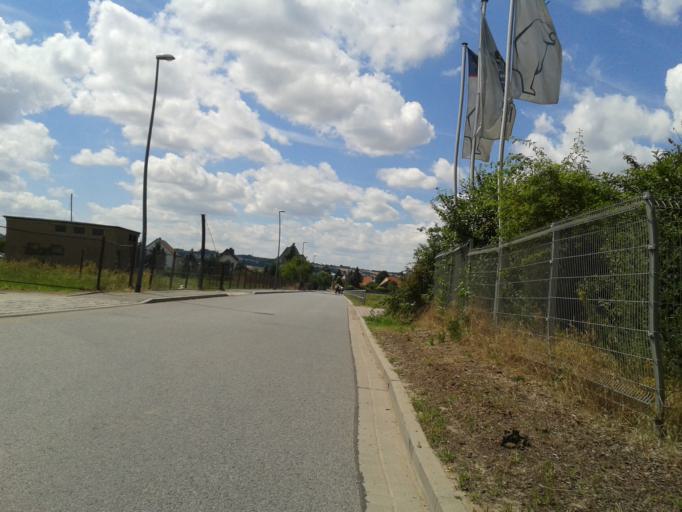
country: DE
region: Saxony
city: Radebeul
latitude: 51.0828
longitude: 13.6806
